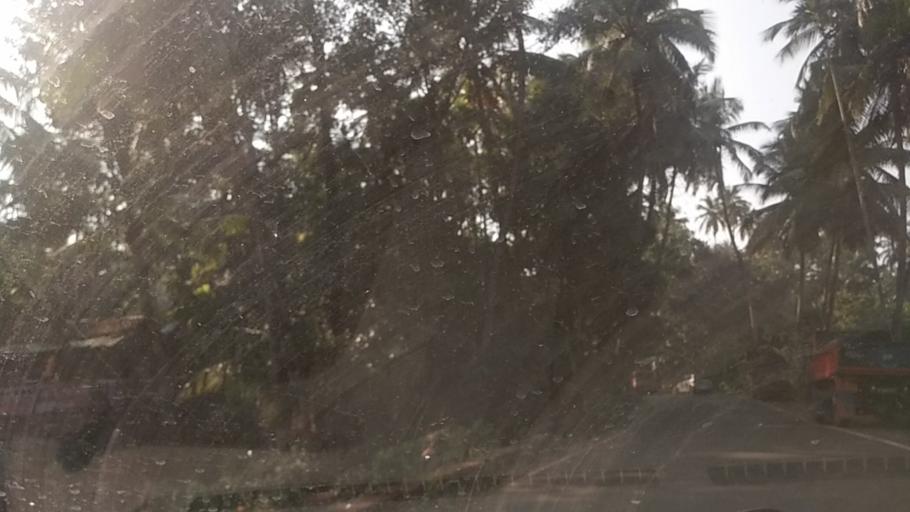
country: IN
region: Goa
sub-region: North Goa
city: Pernem
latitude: 15.7224
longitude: 73.7880
